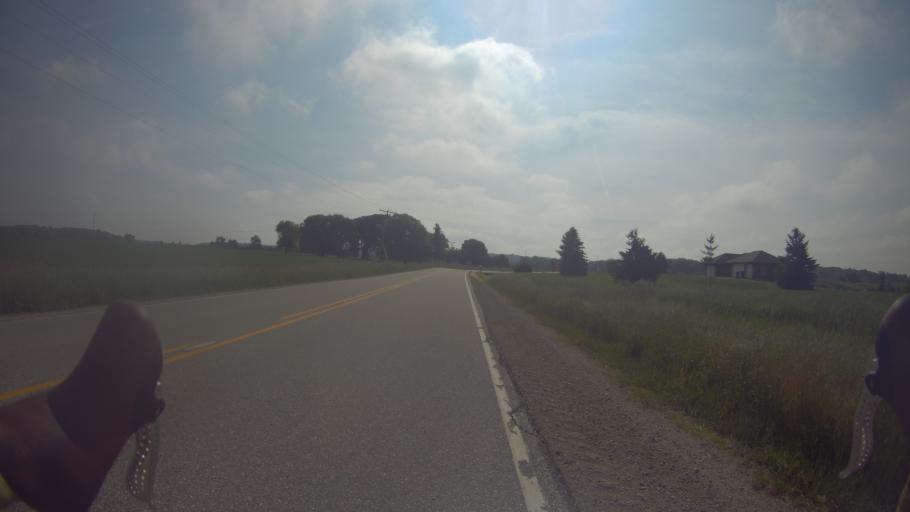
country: US
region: Wisconsin
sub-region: Dane County
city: McFarland
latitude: 43.0150
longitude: -89.2457
